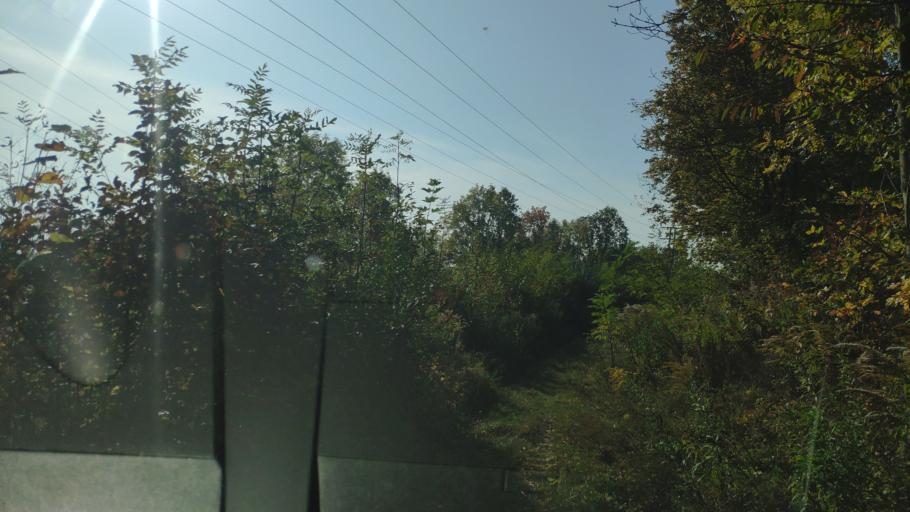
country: SK
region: Kosicky
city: Kosice
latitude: 48.7386
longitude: 21.2324
